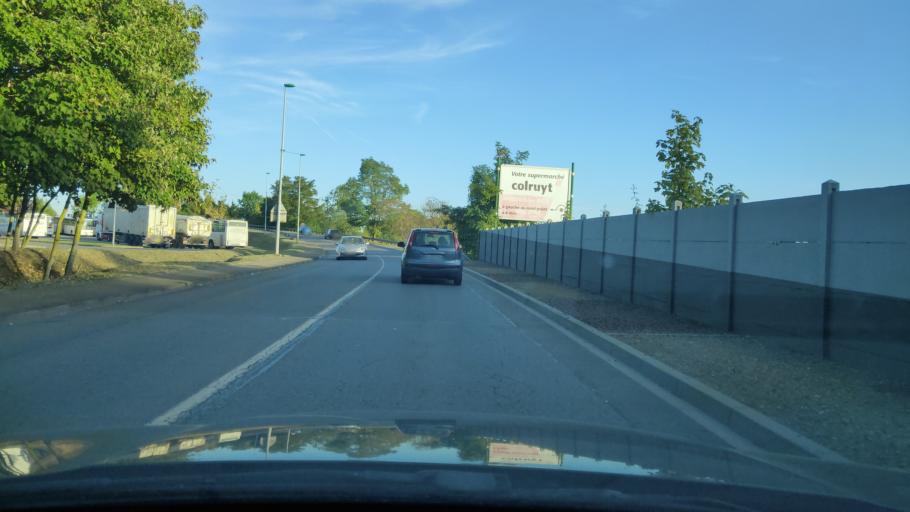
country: FR
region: Lorraine
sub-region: Departement de la Moselle
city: Maizieres-les-Metz
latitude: 49.2116
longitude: 6.1549
